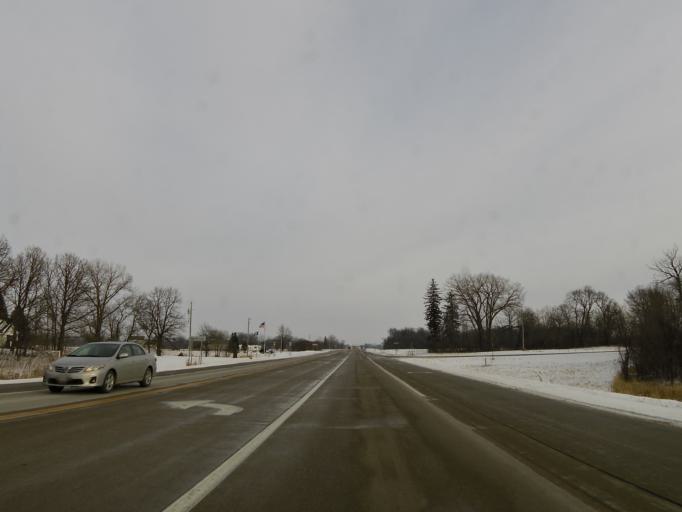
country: US
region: Minnesota
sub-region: McLeod County
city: Hutchinson
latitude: 44.8926
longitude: -94.2752
